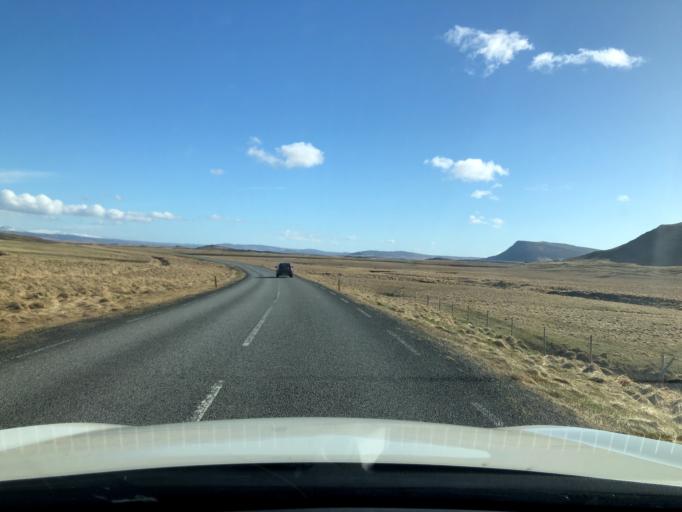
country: IS
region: West
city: Borgarnes
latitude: 64.5730
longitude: -21.6574
